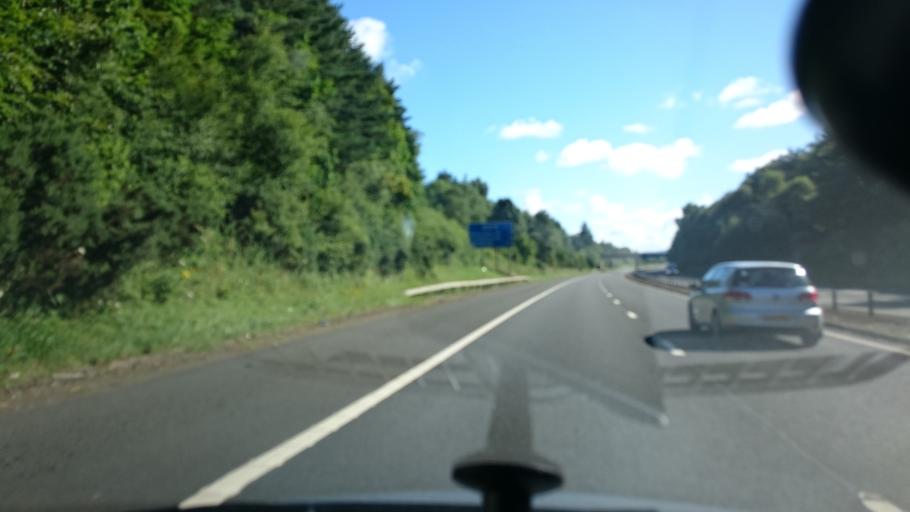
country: GB
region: Scotland
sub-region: Falkirk
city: Larbert
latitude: 56.0311
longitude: -3.8539
